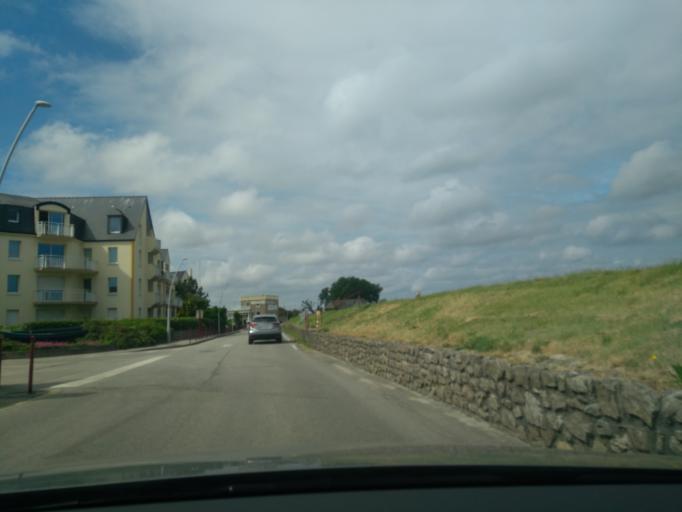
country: FR
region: Lower Normandy
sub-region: Departement de la Manche
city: Saint-Vaast-la-Hougue
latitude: 49.5916
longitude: -1.2667
